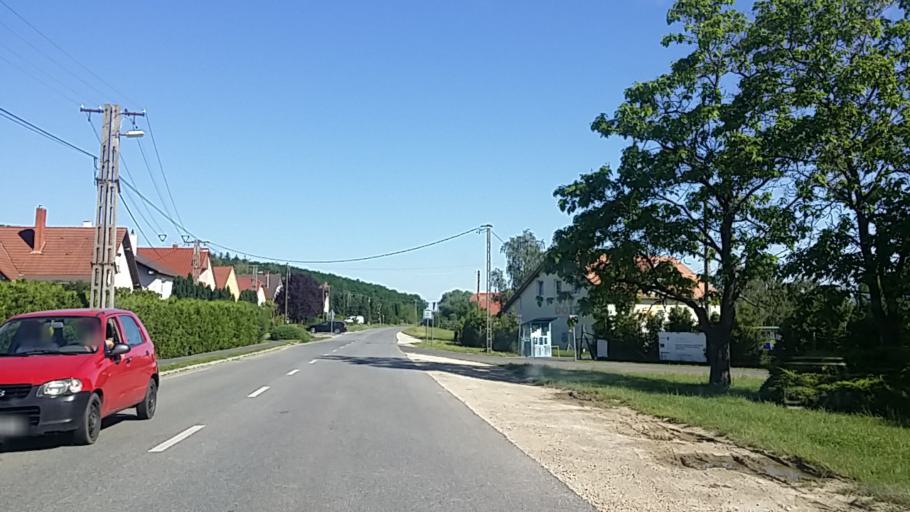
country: HU
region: Zala
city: Zalaegerszeg
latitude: 46.8556
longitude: 16.7805
